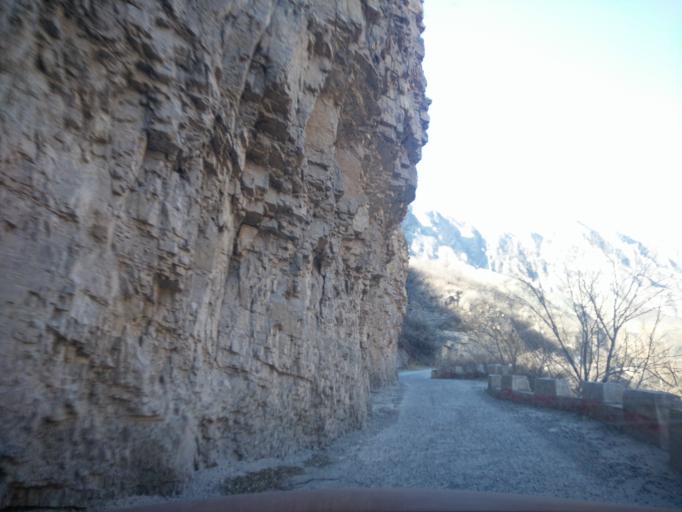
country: CN
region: Beijing
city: Yanjiatai
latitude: 40.1652
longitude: 115.6476
